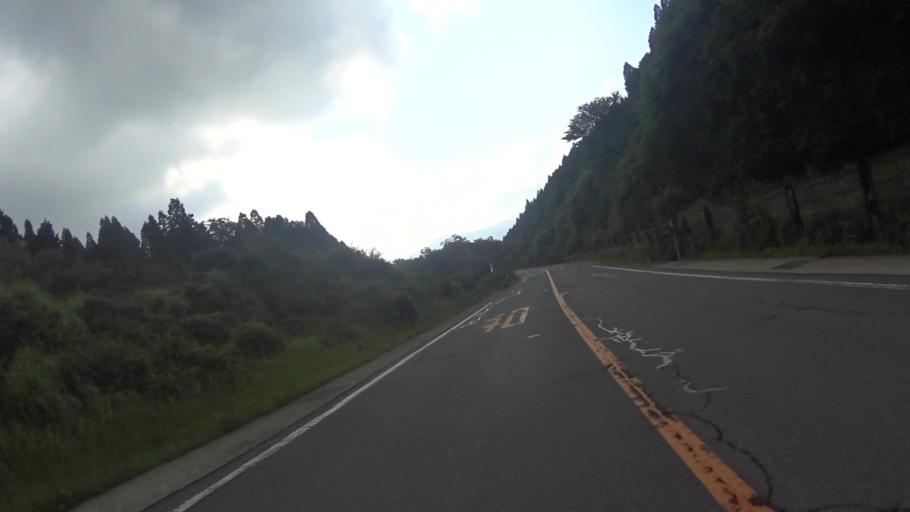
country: JP
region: Kumamoto
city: Aso
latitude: 32.8885
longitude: 131.0539
